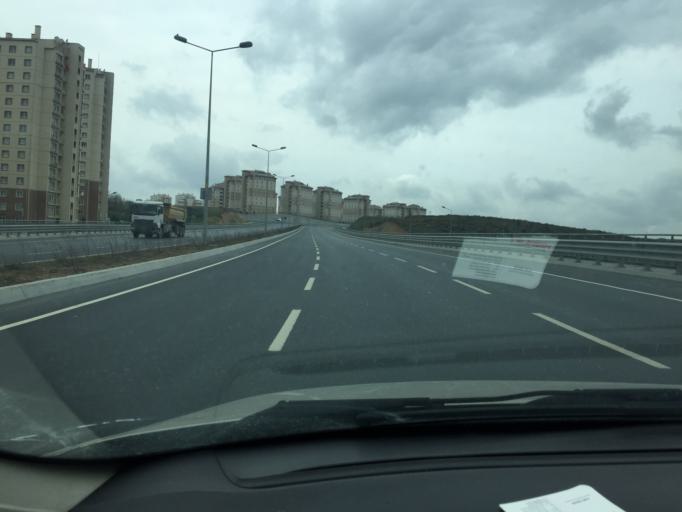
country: TR
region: Istanbul
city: Basaksehir
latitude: 41.1321
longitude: 28.7913
